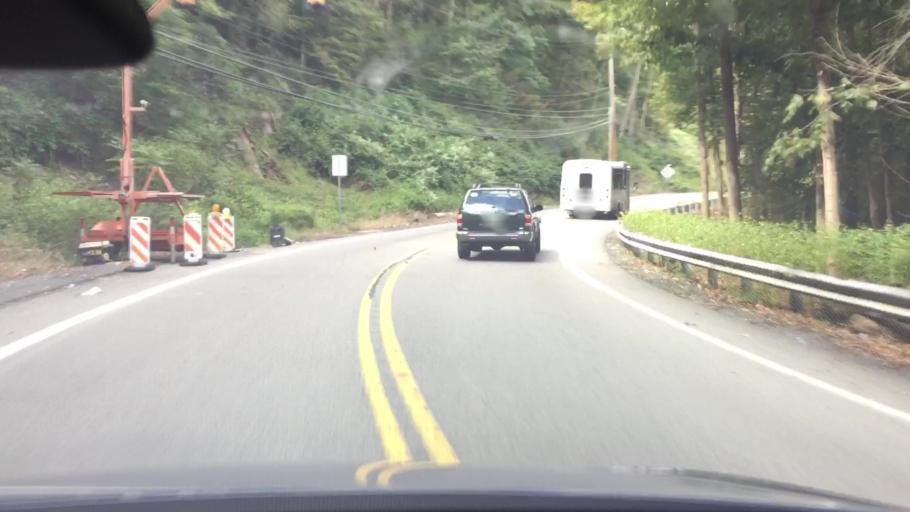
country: US
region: Pennsylvania
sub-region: Allegheny County
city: Cheswick
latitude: 40.5100
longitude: -79.7991
